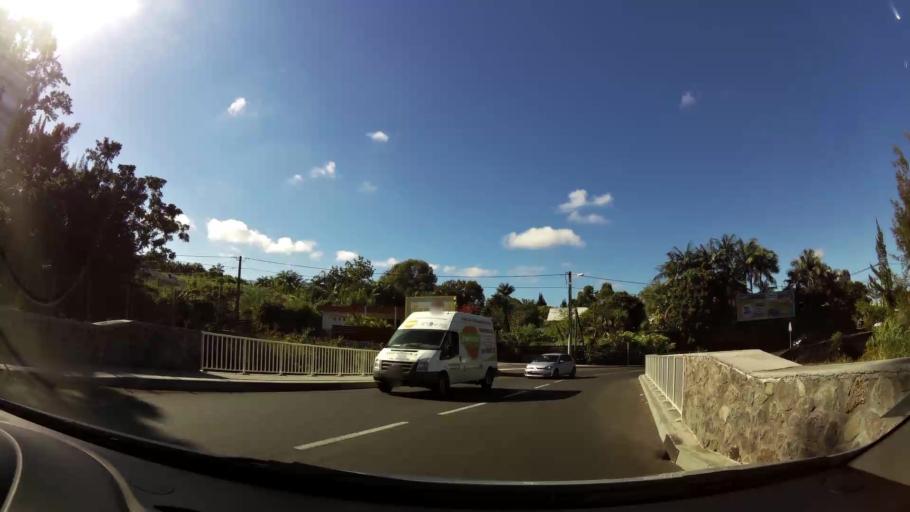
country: RE
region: Reunion
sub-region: Reunion
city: Le Tampon
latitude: -21.2660
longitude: 55.5248
